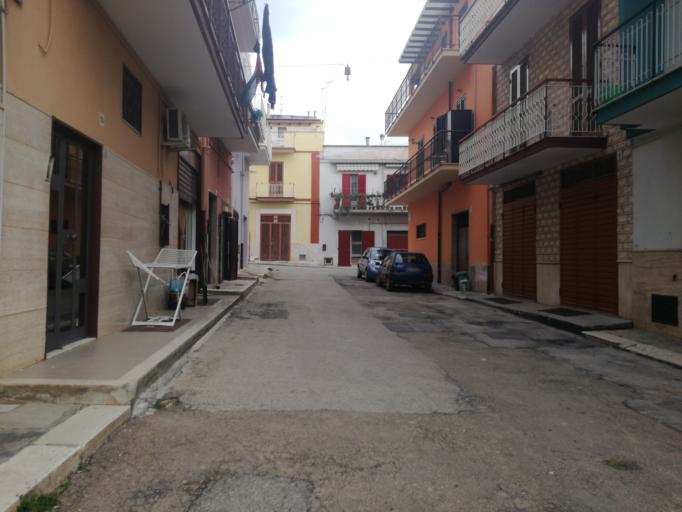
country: IT
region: Apulia
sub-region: Provincia di Bari
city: Ruvo di Puglia
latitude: 41.1183
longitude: 16.4799
